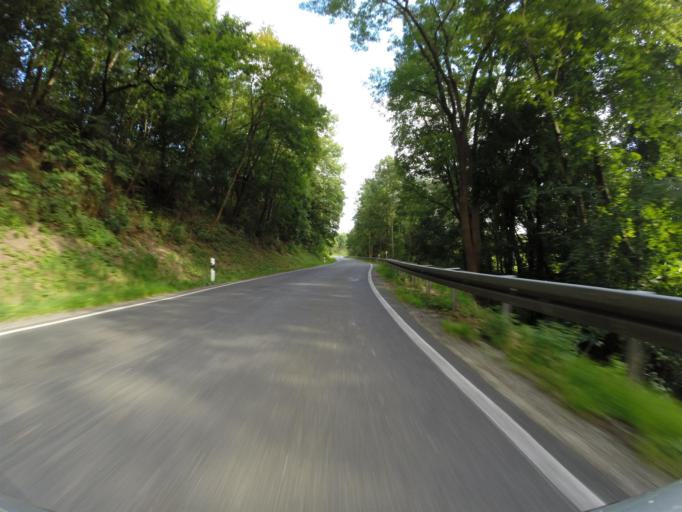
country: DE
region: Thuringia
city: Mellingen
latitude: 50.9376
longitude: 11.4006
